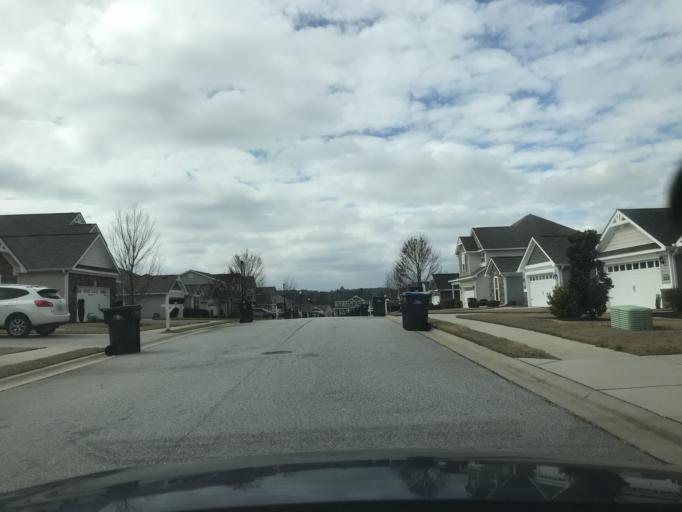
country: US
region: Georgia
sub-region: Columbia County
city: Grovetown
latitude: 33.4397
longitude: -82.1472
